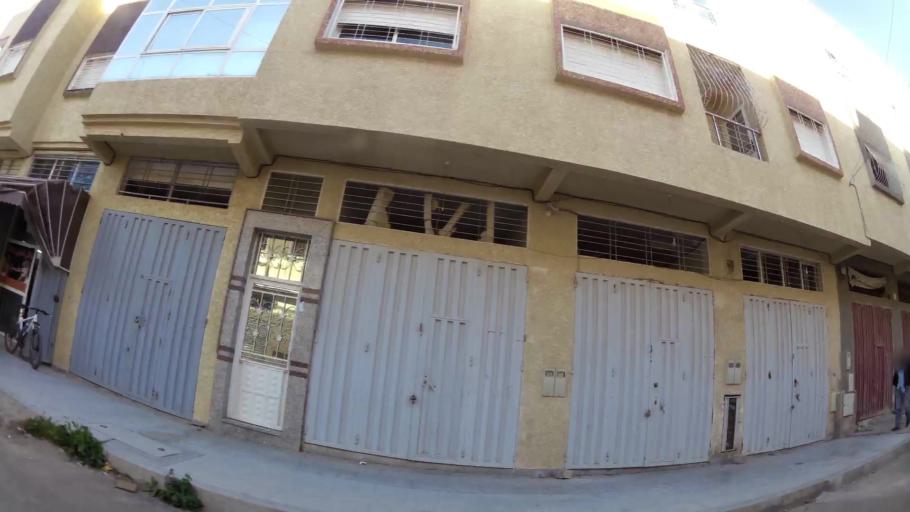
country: MA
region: Fes-Boulemane
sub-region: Fes
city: Fes
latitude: 34.0077
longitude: -5.0141
